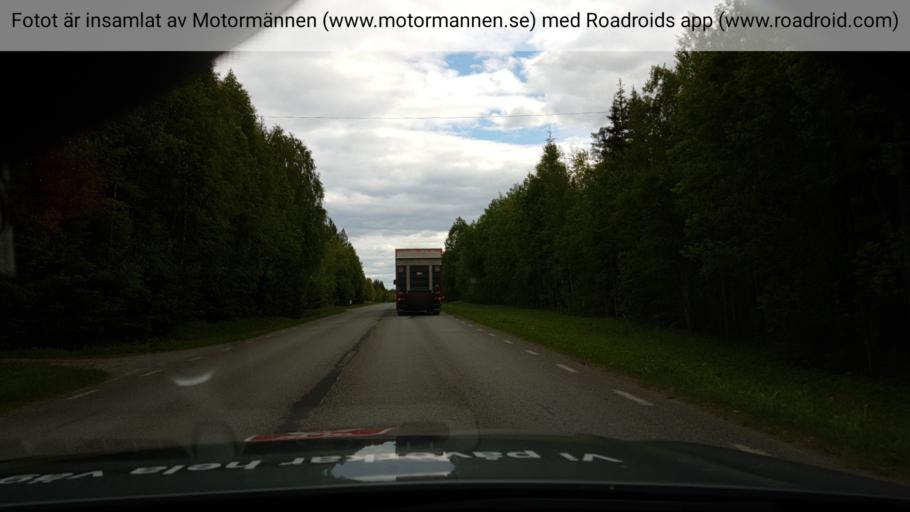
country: SE
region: Jaemtland
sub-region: Stroemsunds Kommun
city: Stroemsund
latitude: 63.8735
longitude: 15.5455
